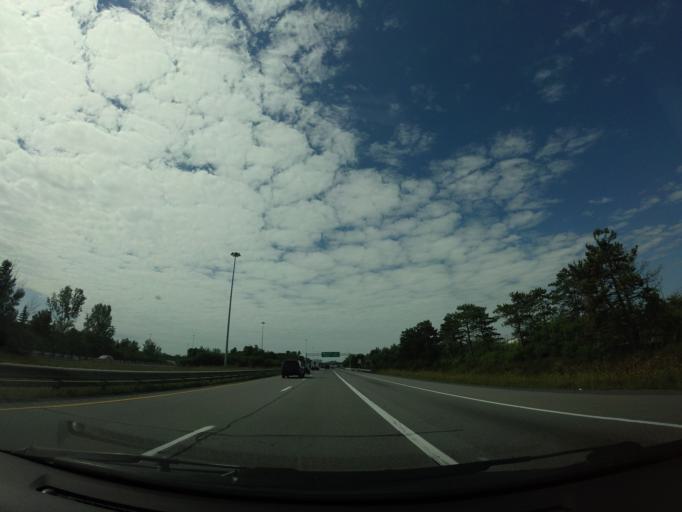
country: CA
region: Ontario
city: Ottawa
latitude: 45.4271
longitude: -75.6151
